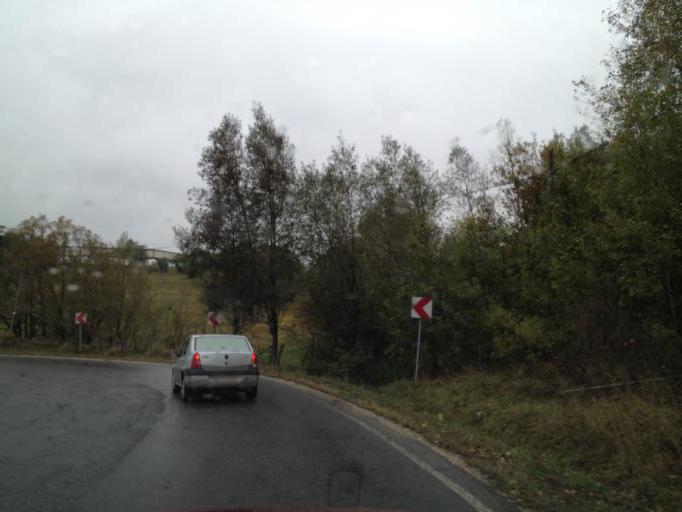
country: RO
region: Arges
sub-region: Comuna Valea Mare-Pravat
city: Valea Mare Pravat
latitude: 45.2920
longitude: 25.1167
